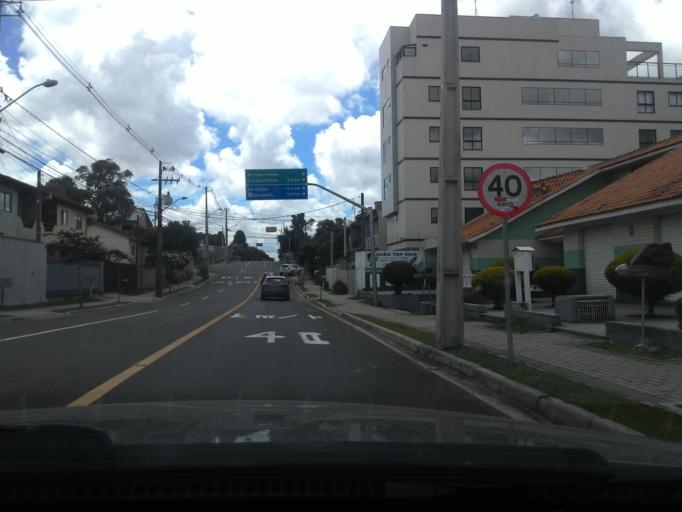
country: BR
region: Parana
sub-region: Pinhais
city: Pinhais
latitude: -25.4687
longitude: -49.2365
